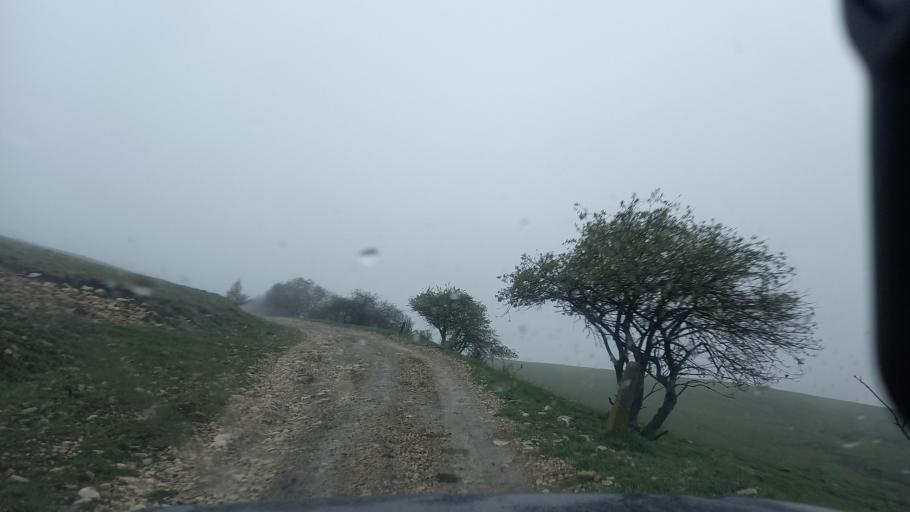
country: RU
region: Kabardino-Balkariya
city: Kamennomostskoye
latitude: 43.6716
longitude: 42.9770
